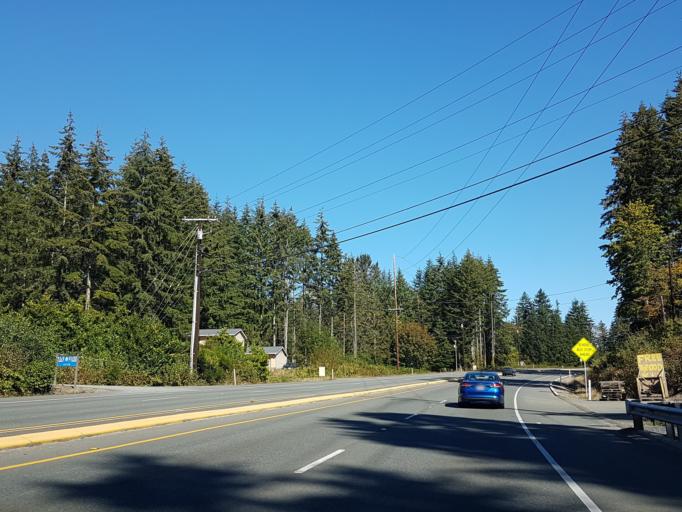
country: US
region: Washington
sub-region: Snohomish County
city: Clearview
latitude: 47.8231
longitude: -122.1360
